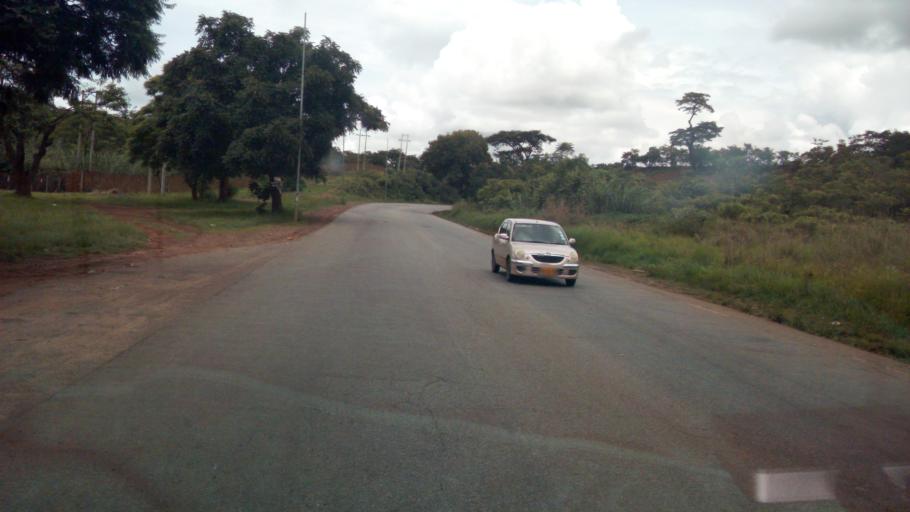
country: ZW
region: Harare
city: Harare
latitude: -17.8166
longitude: 31.0005
